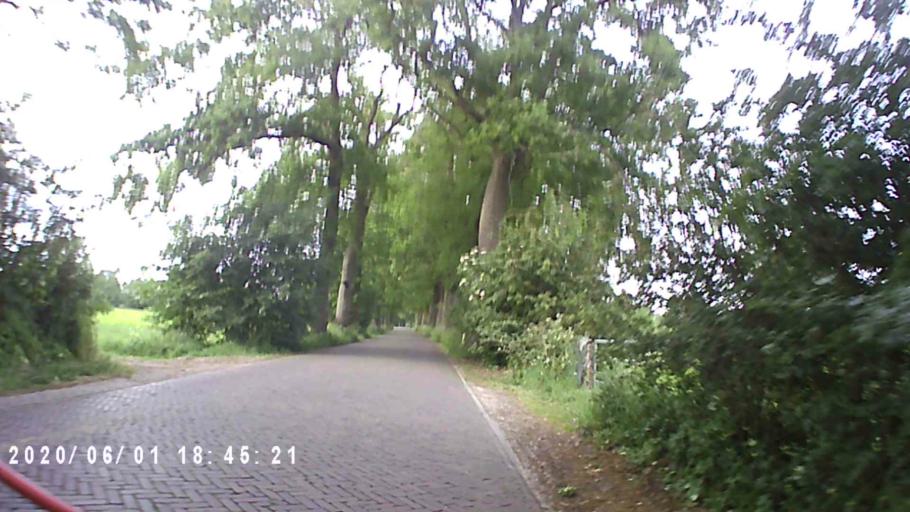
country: NL
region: Friesland
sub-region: Gemeente Tytsjerksteradiel
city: Eastermar
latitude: 53.1784
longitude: 6.0678
